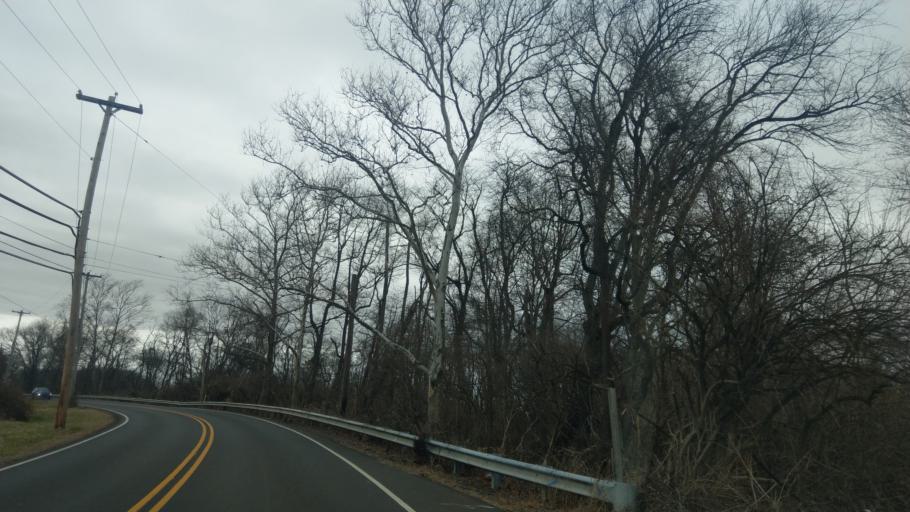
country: US
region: Pennsylvania
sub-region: Bucks County
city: Hulmeville
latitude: 40.1279
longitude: -74.9208
